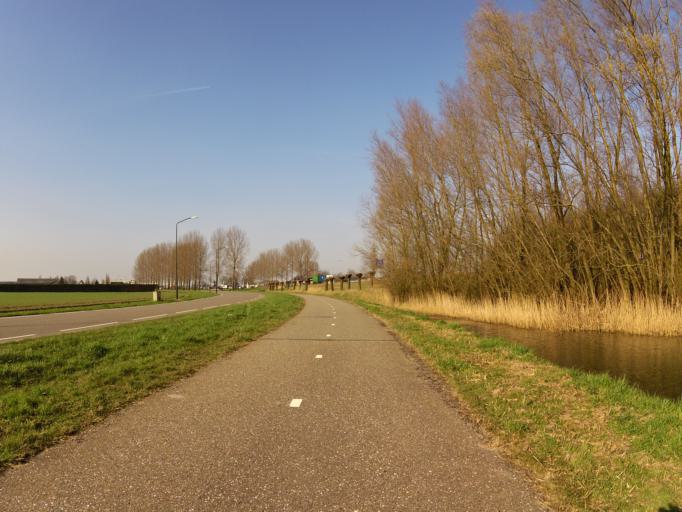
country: NL
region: North Brabant
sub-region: Gemeente Aalburg
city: Aalburg
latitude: 51.7423
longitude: 5.1143
